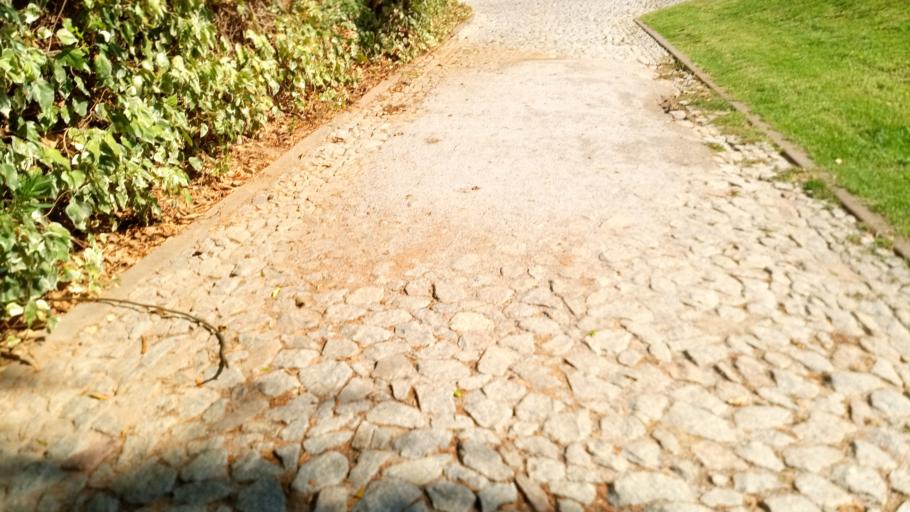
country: PT
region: Evora
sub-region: Portel
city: Portel
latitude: 38.3097
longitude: -7.7025
